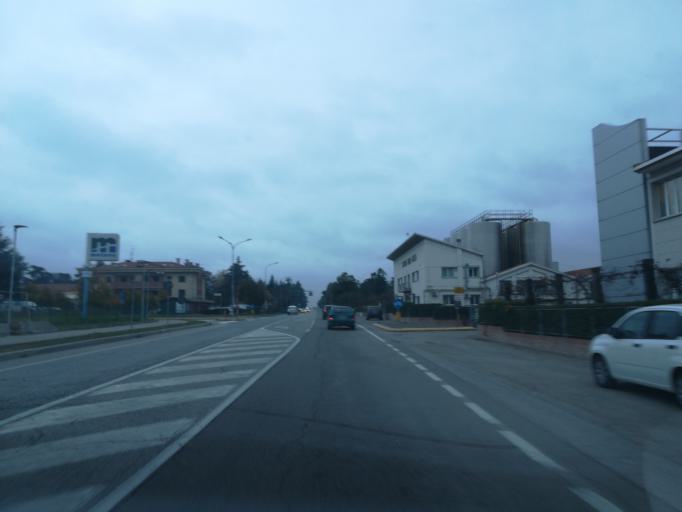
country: IT
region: Emilia-Romagna
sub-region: Provincia di Bologna
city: Toscanella
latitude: 44.3750
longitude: 11.6590
